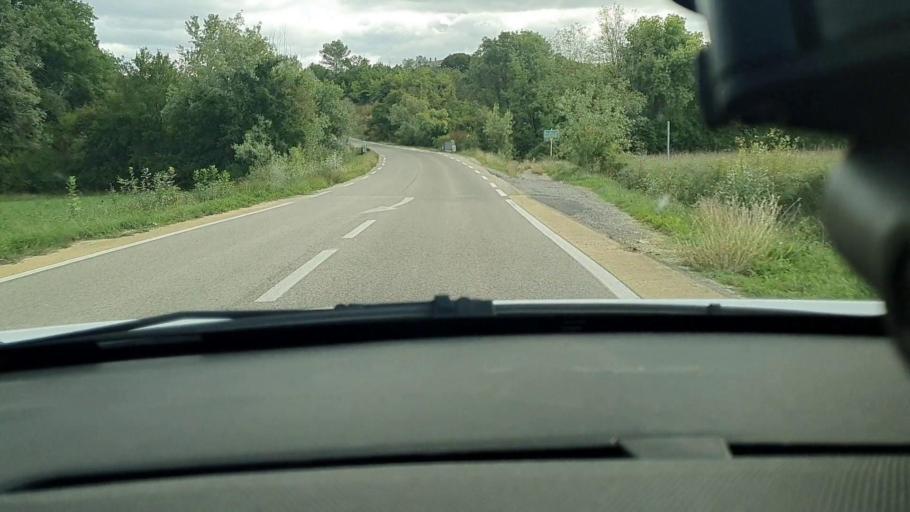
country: FR
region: Languedoc-Roussillon
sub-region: Departement du Gard
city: Salindres
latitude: 44.1893
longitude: 4.2188
